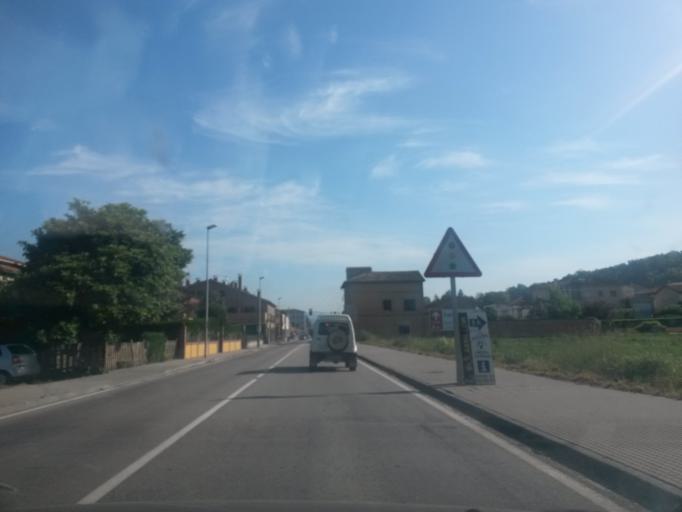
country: ES
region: Catalonia
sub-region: Provincia de Girona
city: Bas
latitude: 42.1426
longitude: 2.4577
